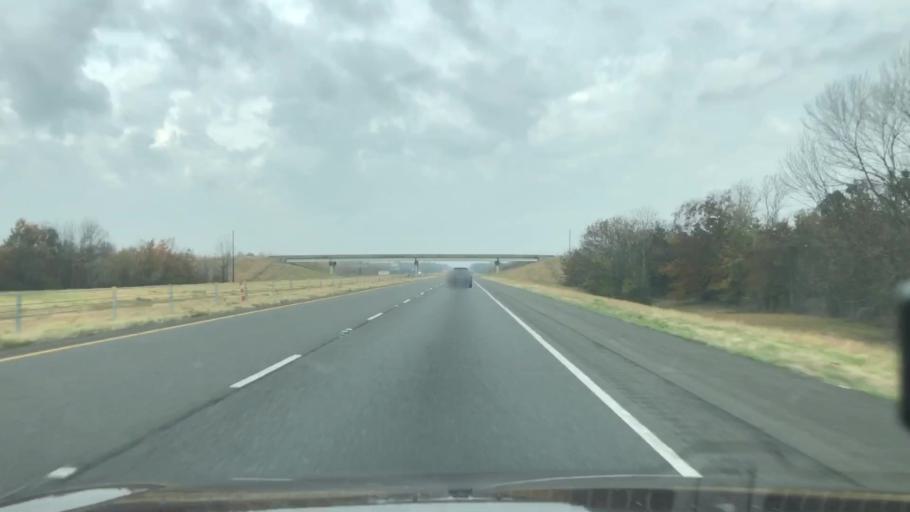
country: US
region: Louisiana
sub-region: Richland Parish
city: Delhi
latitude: 32.4370
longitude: -91.4552
